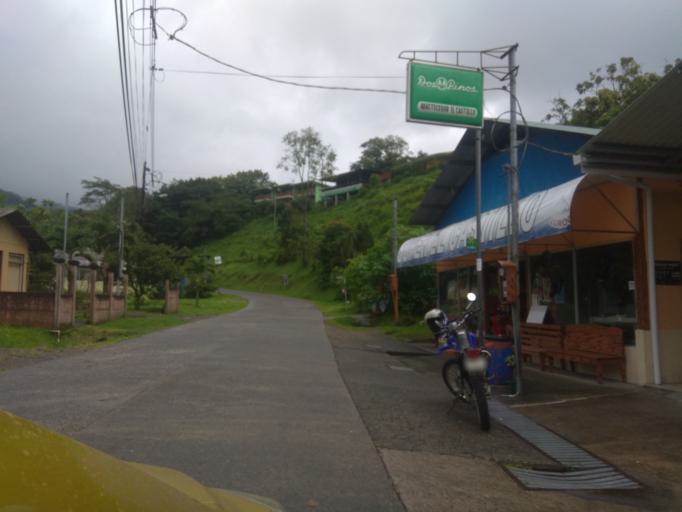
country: CR
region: Alajuela
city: La Fortuna
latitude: 10.4269
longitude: -84.7506
